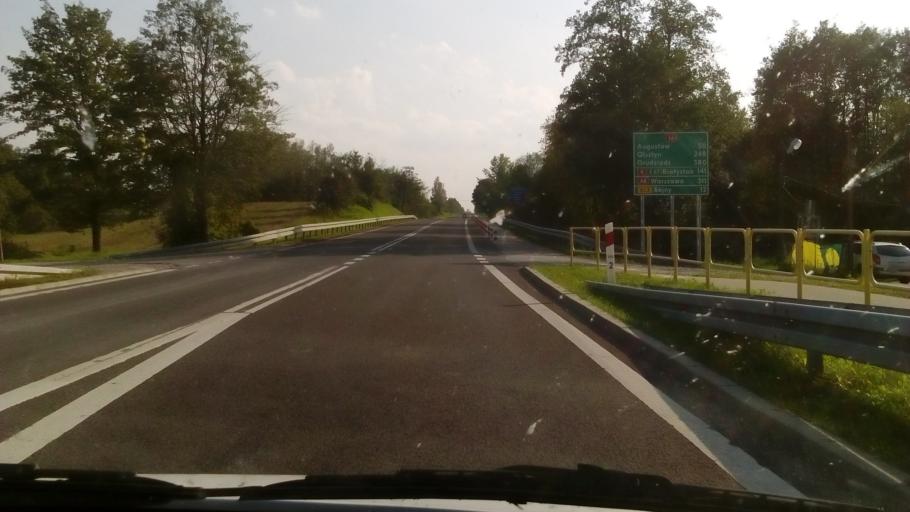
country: LT
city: Lazdijai
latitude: 54.1565
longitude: 23.4724
